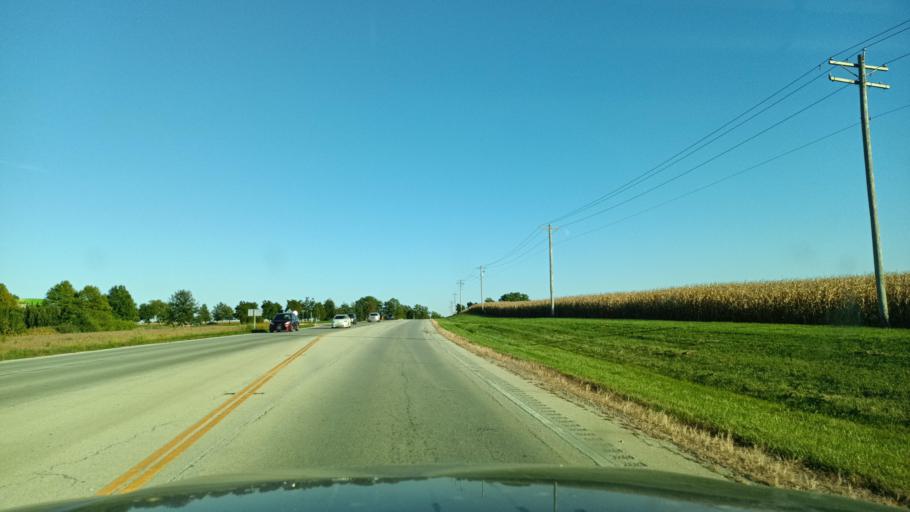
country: US
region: Illinois
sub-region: Champaign County
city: Lake of the Woods
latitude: 40.1840
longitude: -88.3643
